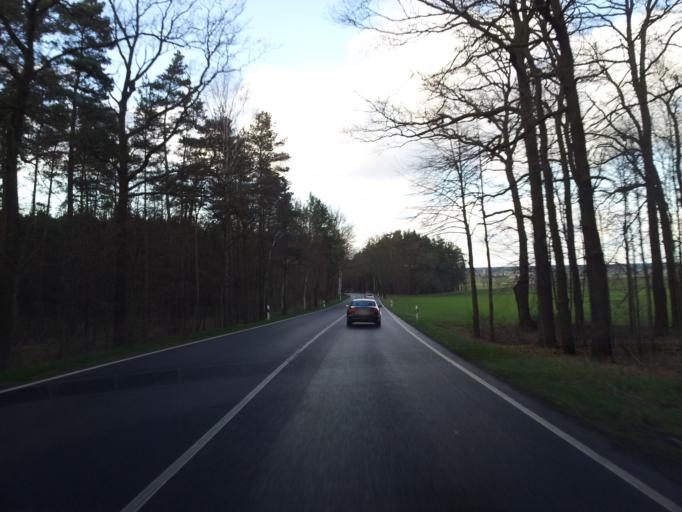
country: DE
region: Saxony
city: Konigsbruck
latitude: 51.2760
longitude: 13.9070
